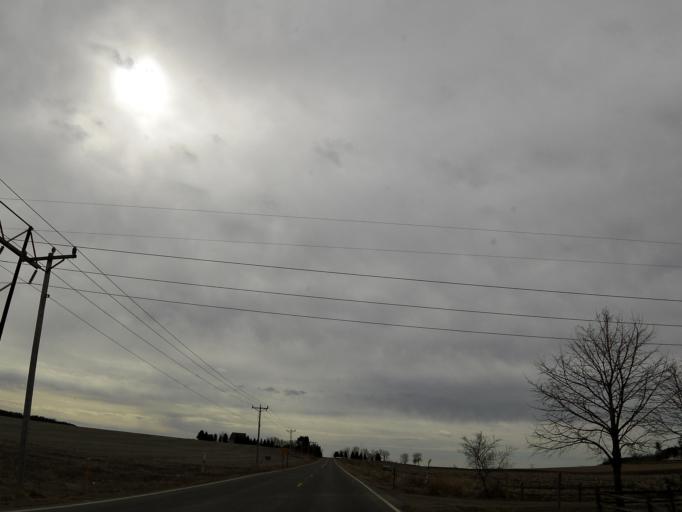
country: US
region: Minnesota
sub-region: Washington County
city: Afton
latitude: 44.8838
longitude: -92.8428
